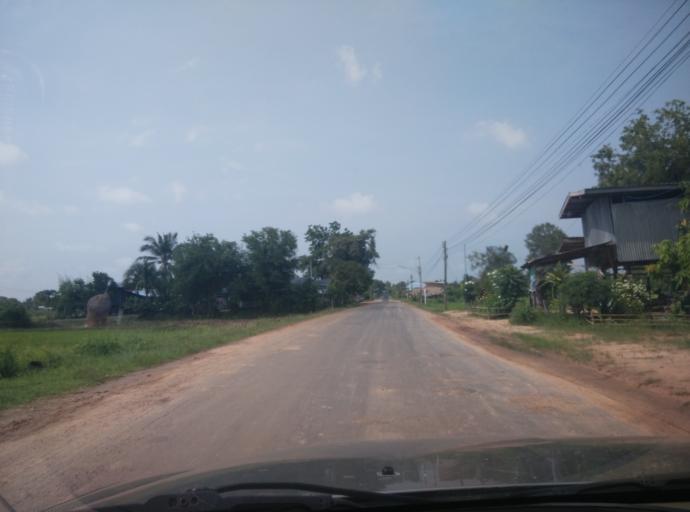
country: TH
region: Sisaket
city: Huai Thap Than
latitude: 15.0117
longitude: 104.0697
